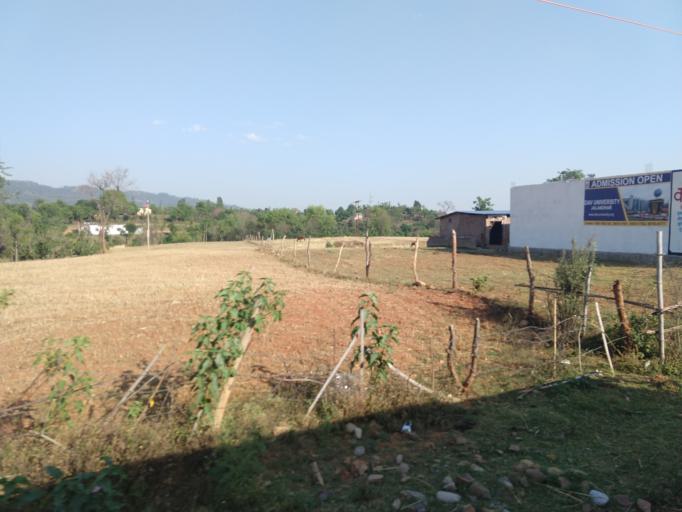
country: IN
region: Himachal Pradesh
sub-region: Chamba
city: Chowari
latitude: 32.3716
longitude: 75.9226
